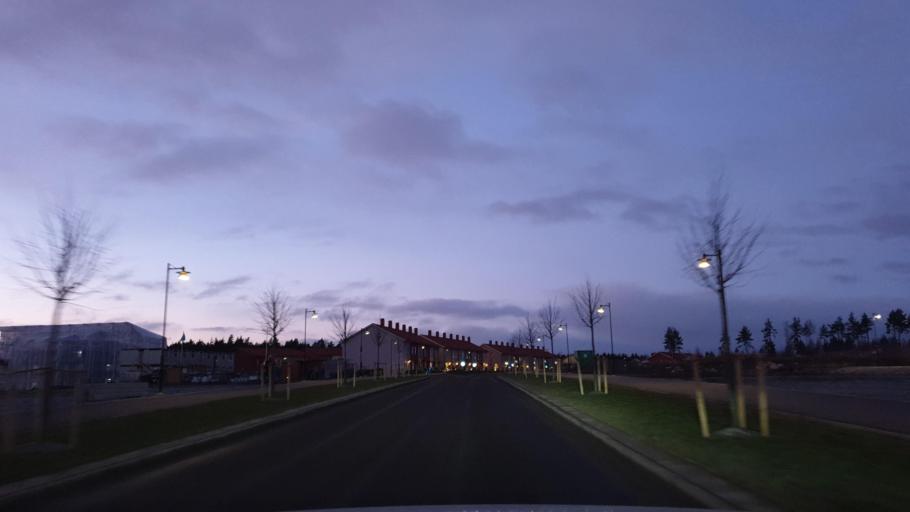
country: SE
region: Stockholm
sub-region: Sigtuna Kommun
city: Marsta
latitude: 59.6077
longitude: 17.7970
